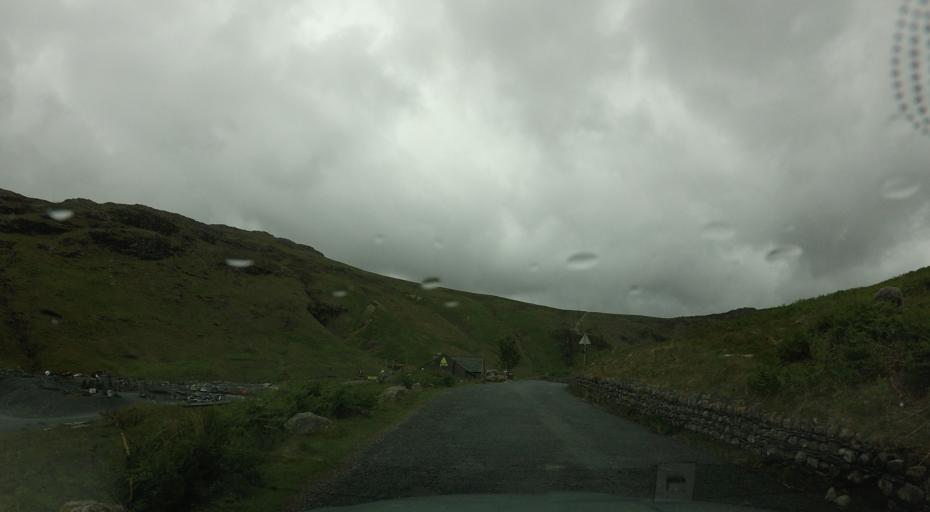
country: GB
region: England
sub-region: Cumbria
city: Keswick
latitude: 54.5118
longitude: -3.1965
